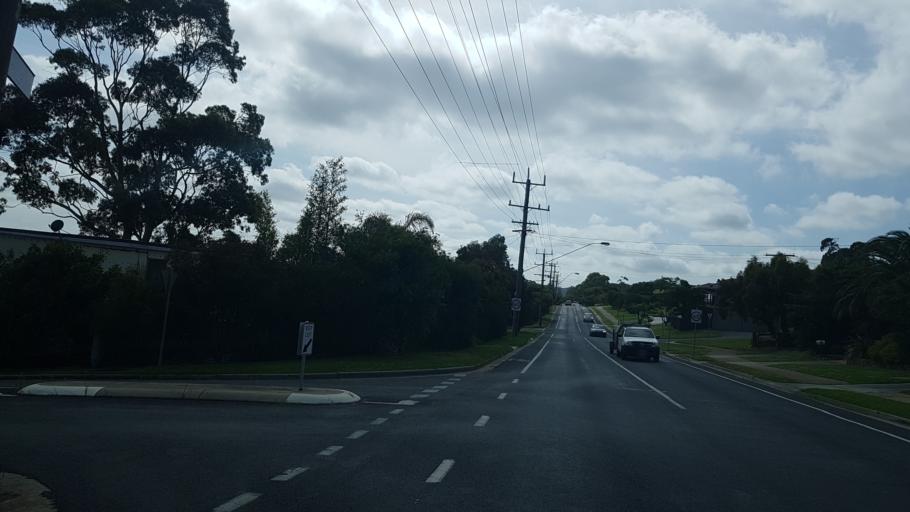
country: AU
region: Victoria
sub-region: Mornington Peninsula
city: Dromana
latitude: -38.3432
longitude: 144.9731
